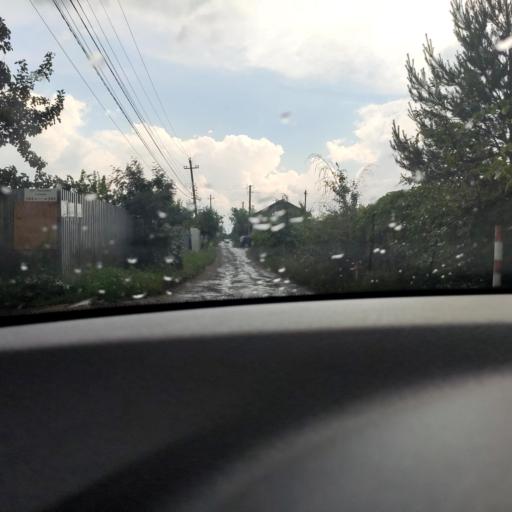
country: RU
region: Samara
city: Novosemeykino
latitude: 53.4010
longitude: 50.3144
